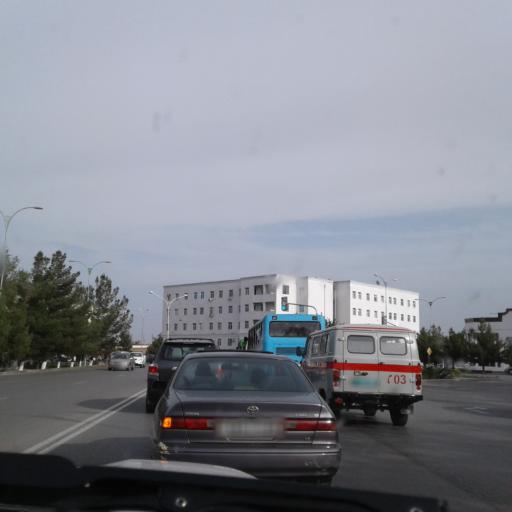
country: TM
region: Mary
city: Mary
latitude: 37.5876
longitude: 61.8408
